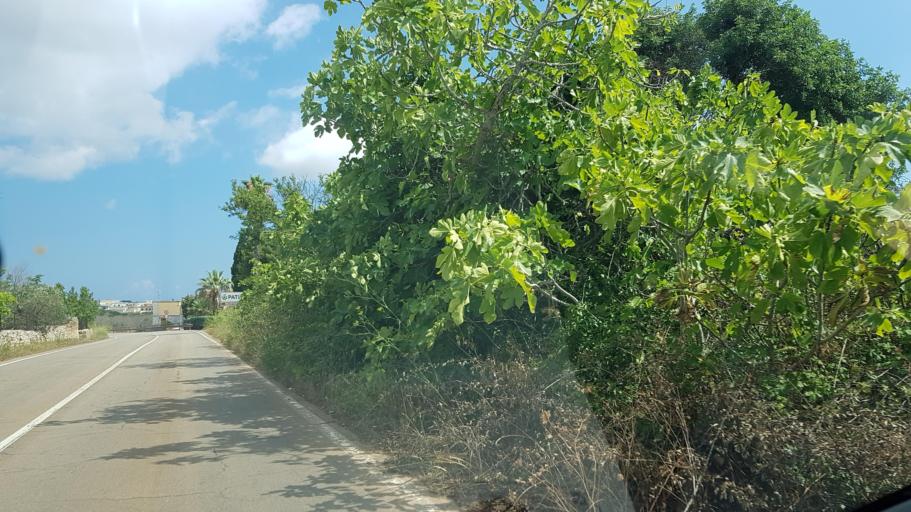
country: IT
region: Apulia
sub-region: Provincia di Lecce
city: Patu
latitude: 39.8440
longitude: 18.3291
